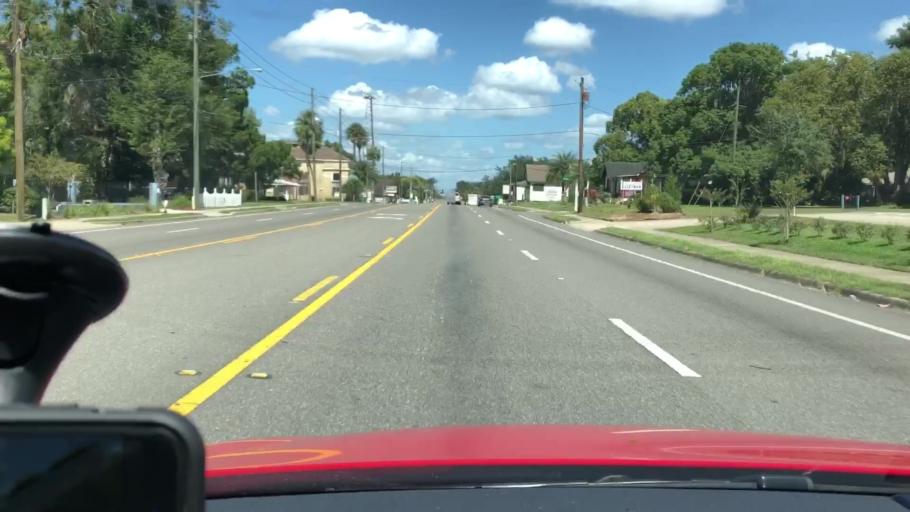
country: US
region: Florida
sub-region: Volusia County
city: Orange City
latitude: 28.9460
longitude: -81.2988
